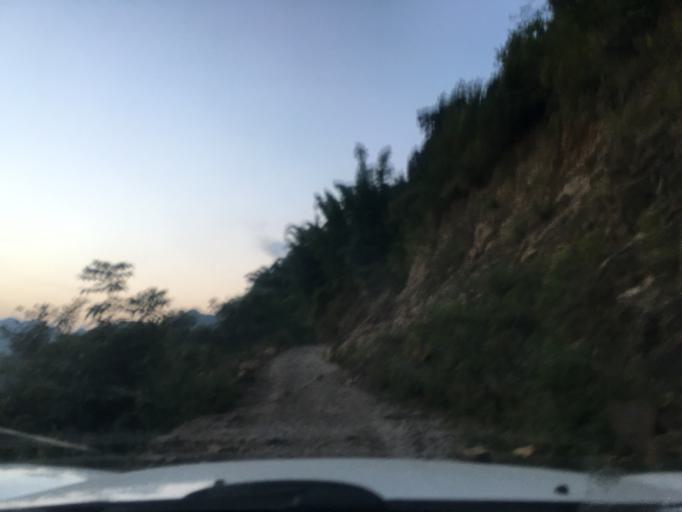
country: CN
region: Guangxi Zhuangzu Zizhiqu
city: Xinzhou
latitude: 25.3550
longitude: 105.7436
